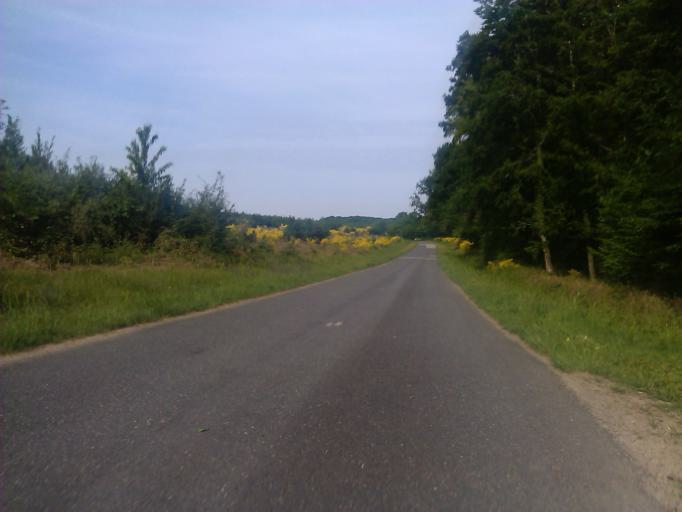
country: FR
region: Auvergne
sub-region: Departement de l'Allier
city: Cerilly
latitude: 46.6144
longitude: 2.7327
